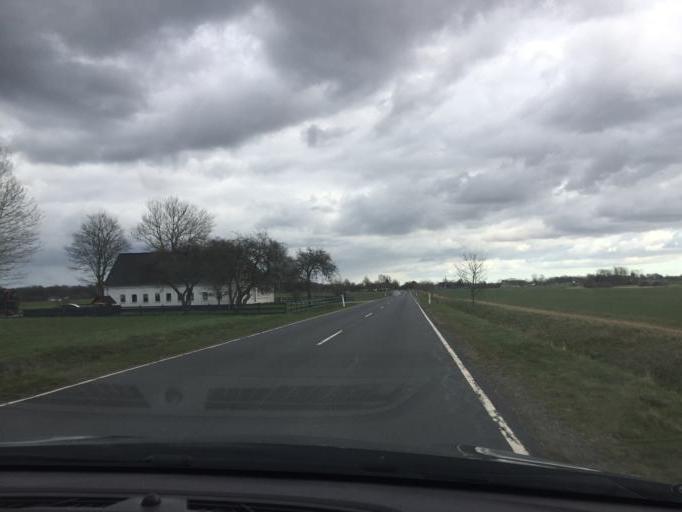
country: DK
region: South Denmark
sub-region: Kerteminde Kommune
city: Langeskov
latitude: 55.2976
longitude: 10.6011
